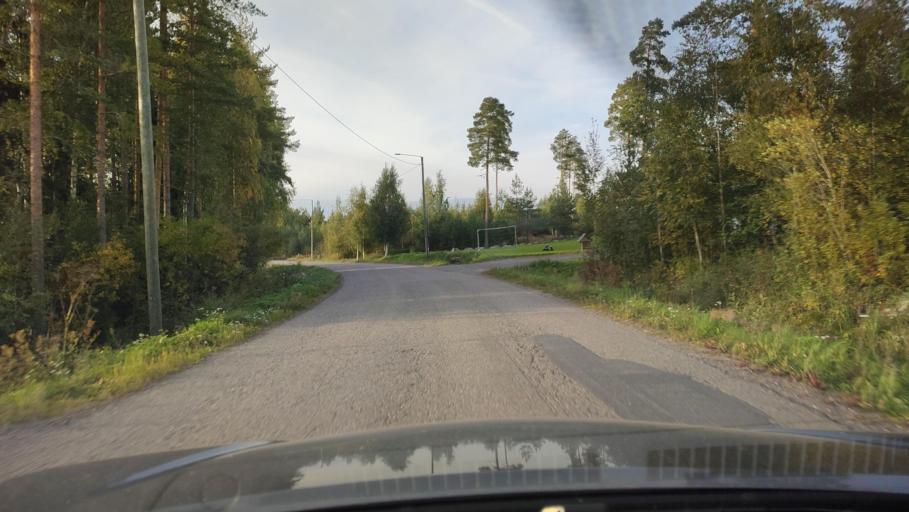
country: FI
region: Southern Ostrobothnia
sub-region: Suupohja
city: Karijoki
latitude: 62.1433
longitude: 21.5684
